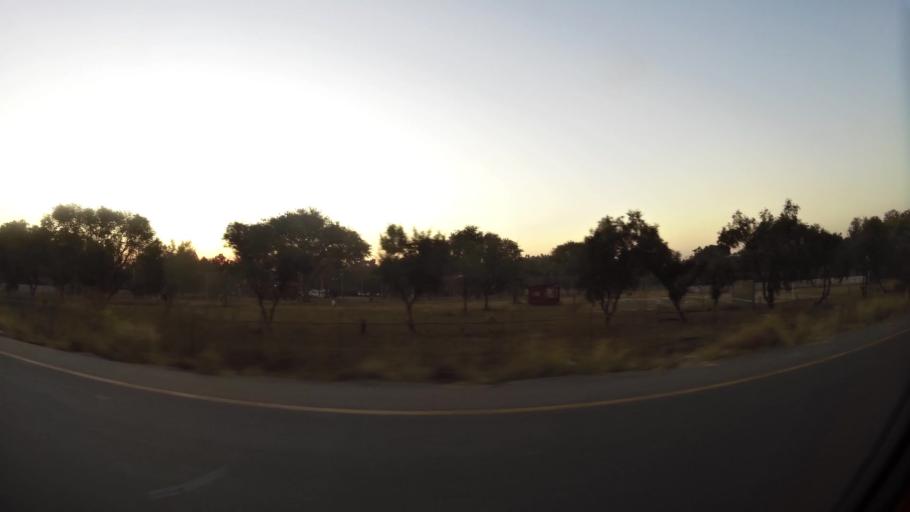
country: ZA
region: North-West
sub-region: Bojanala Platinum District Municipality
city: Rustenburg
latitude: -25.6450
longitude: 27.2584
